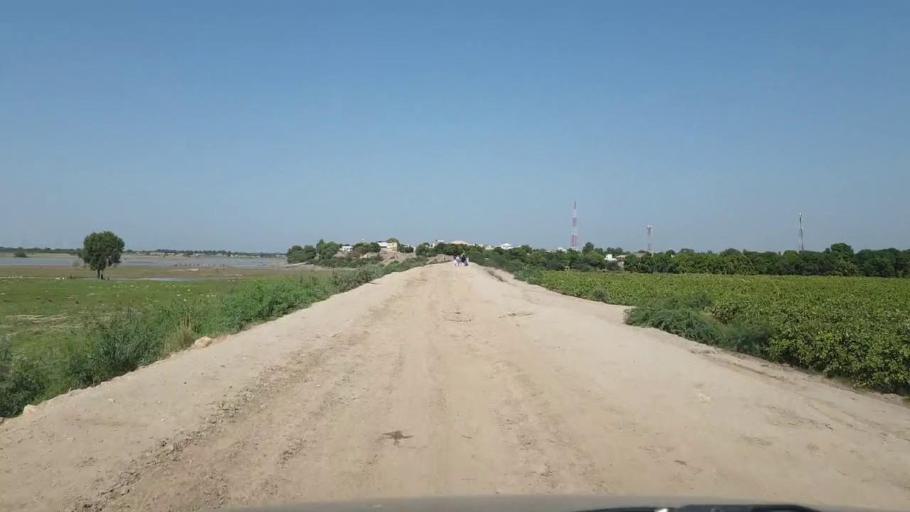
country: PK
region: Sindh
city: Matiari
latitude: 25.6450
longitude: 68.4930
